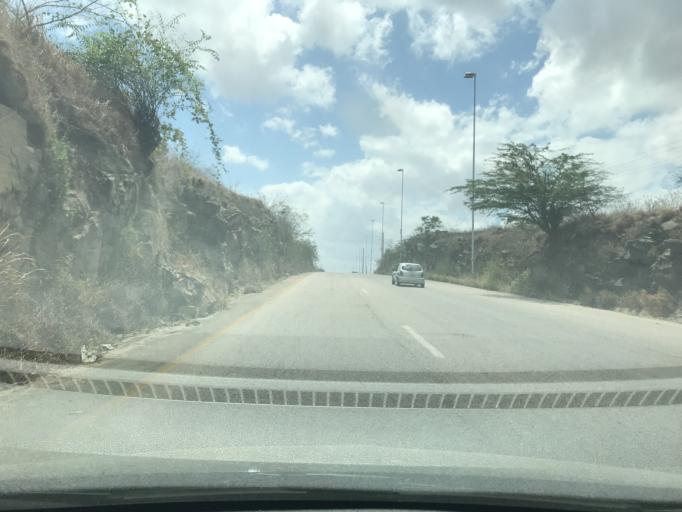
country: BR
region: Pernambuco
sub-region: Caruaru
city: Caruaru
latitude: -8.3059
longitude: -35.9648
